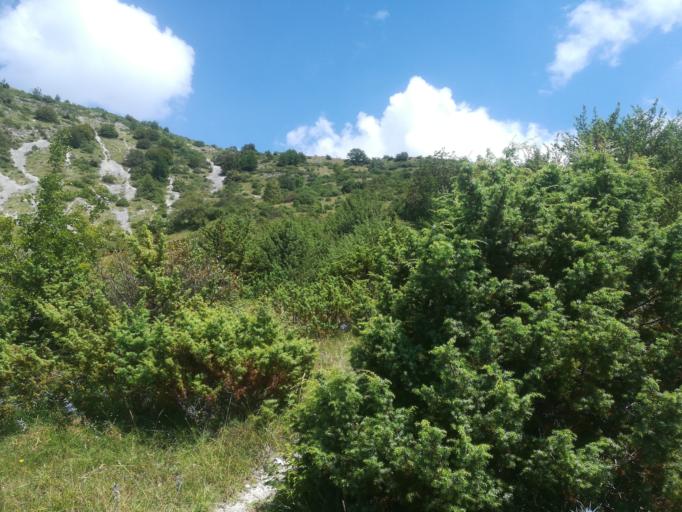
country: IT
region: Umbria
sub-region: Provincia di Perugia
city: Scheggino
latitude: 42.6752
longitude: 12.8583
